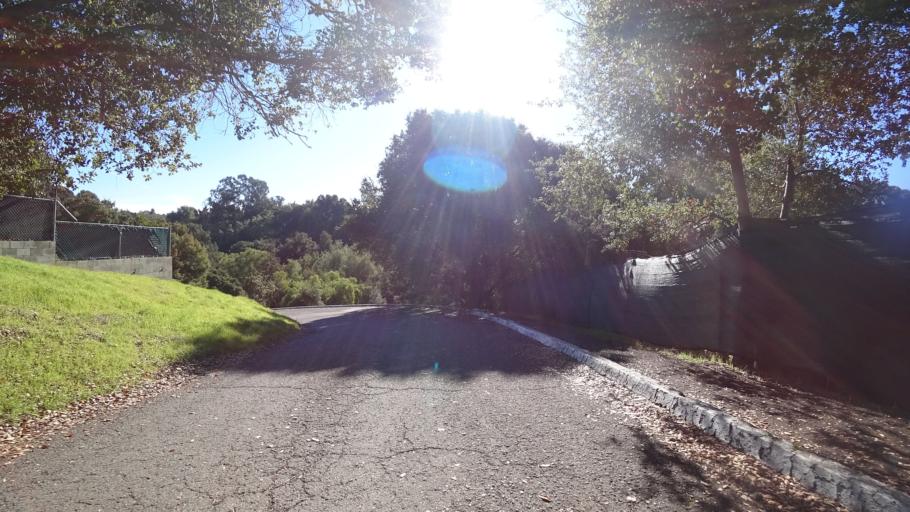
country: US
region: California
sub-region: Alameda County
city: Hayward
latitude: 37.6775
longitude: -122.0647
